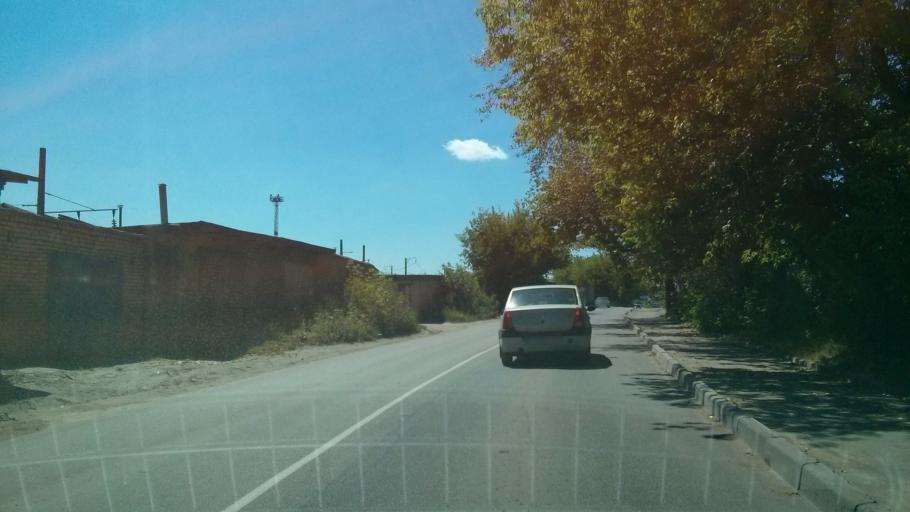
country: RU
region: Vladimir
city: Murom
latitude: 55.5647
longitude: 42.0392
